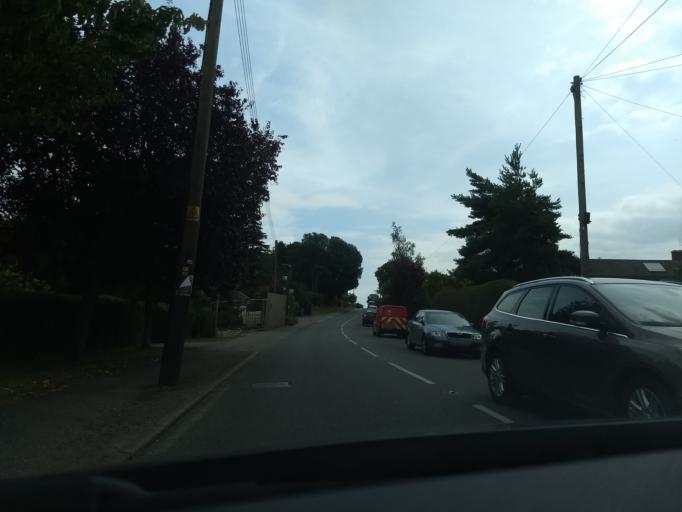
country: GB
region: England
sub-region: Suffolk
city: Shotley Gate
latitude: 51.9894
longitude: 1.2104
